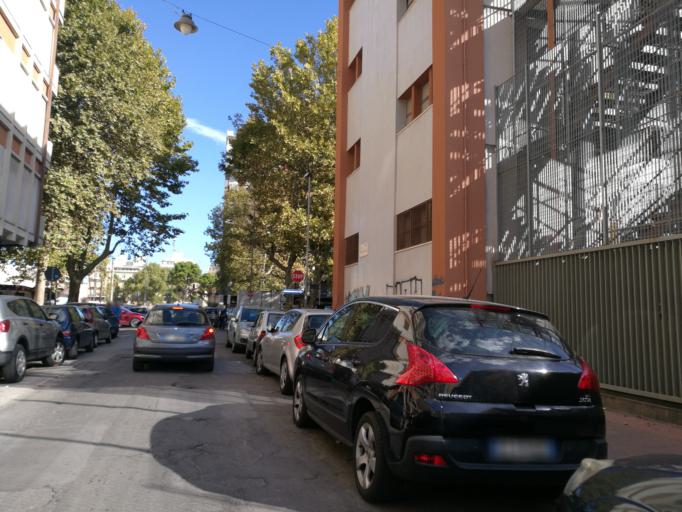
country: IT
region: Apulia
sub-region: Provincia di Bari
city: Bari
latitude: 41.1247
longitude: 16.8550
